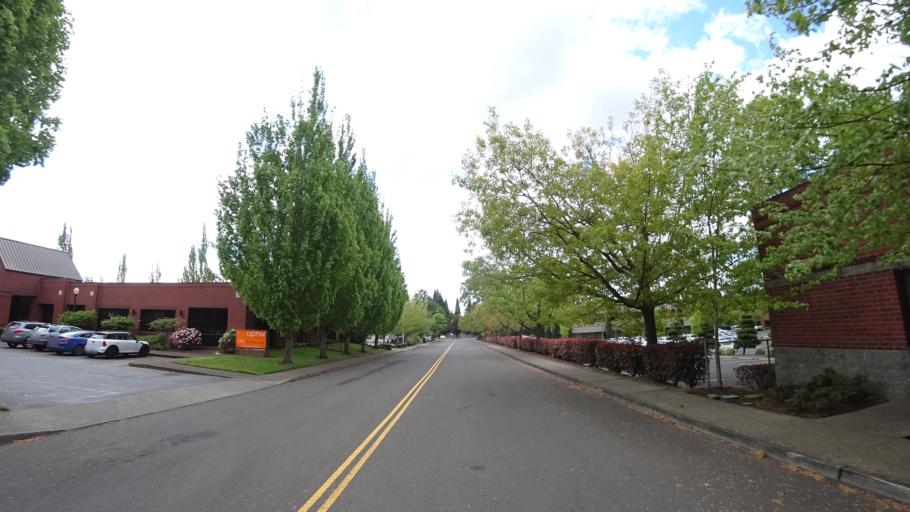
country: US
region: Oregon
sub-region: Washington County
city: Metzger
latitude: 45.4291
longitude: -122.7469
